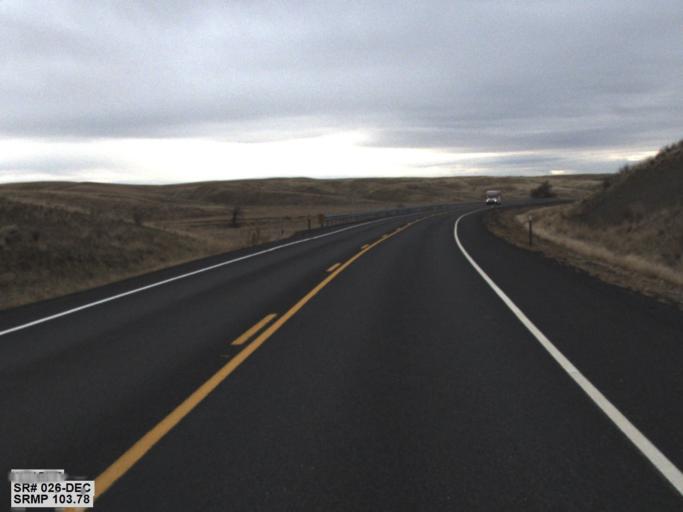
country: US
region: Washington
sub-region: Garfield County
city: Pomeroy
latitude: 46.7848
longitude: -117.9142
